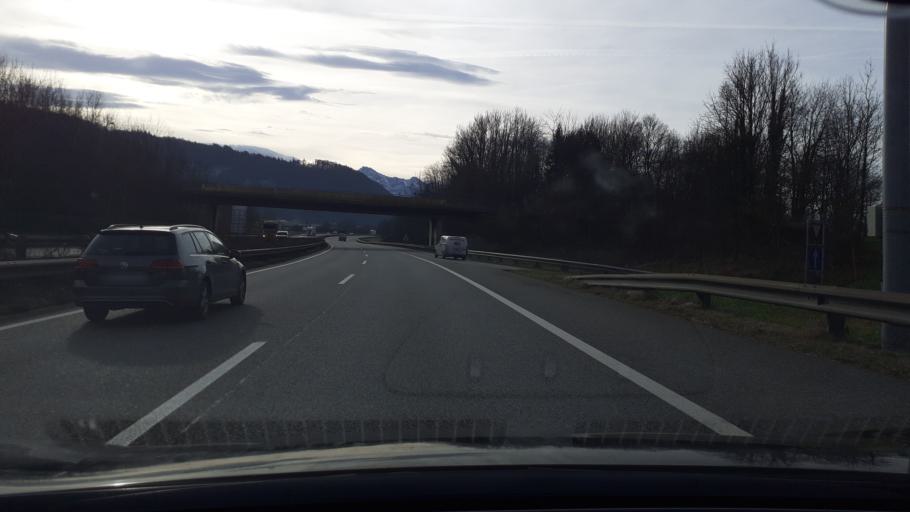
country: AT
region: Vorarlberg
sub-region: Politischer Bezirk Feldkirch
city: Gotzis
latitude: 47.3321
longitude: 9.6278
